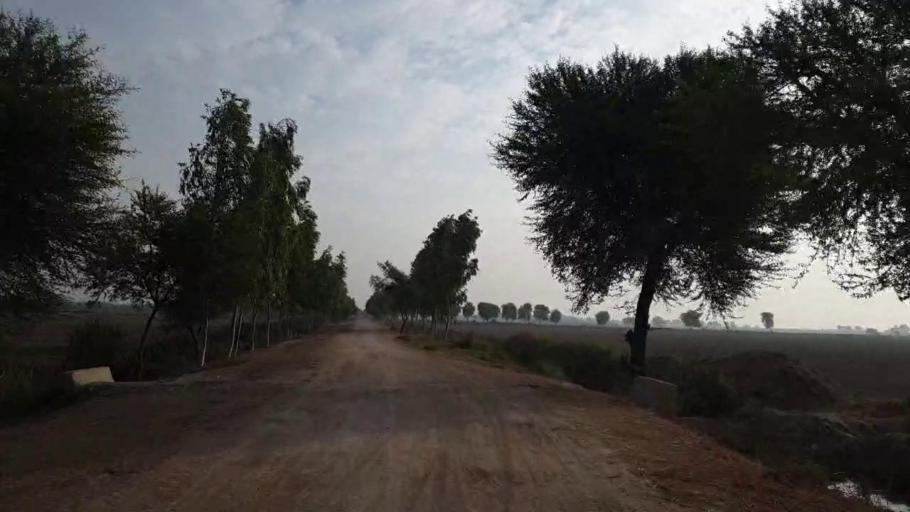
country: PK
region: Sindh
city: Tando Muhammad Khan
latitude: 25.1113
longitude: 68.4314
